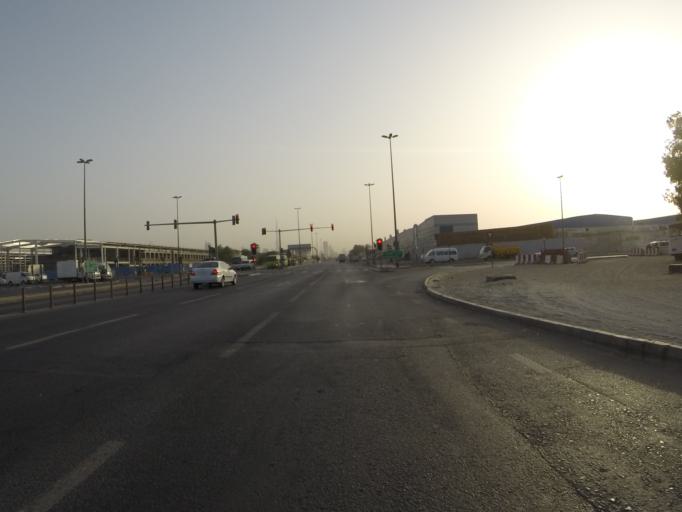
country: AE
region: Dubai
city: Dubai
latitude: 25.1388
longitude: 55.2398
